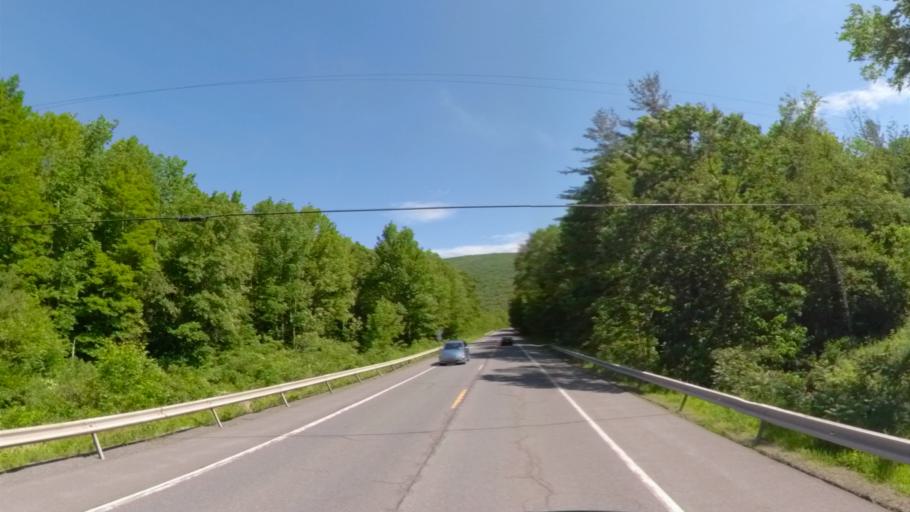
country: US
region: New York
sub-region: Ulster County
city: Shokan
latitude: 42.1112
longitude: -74.4293
